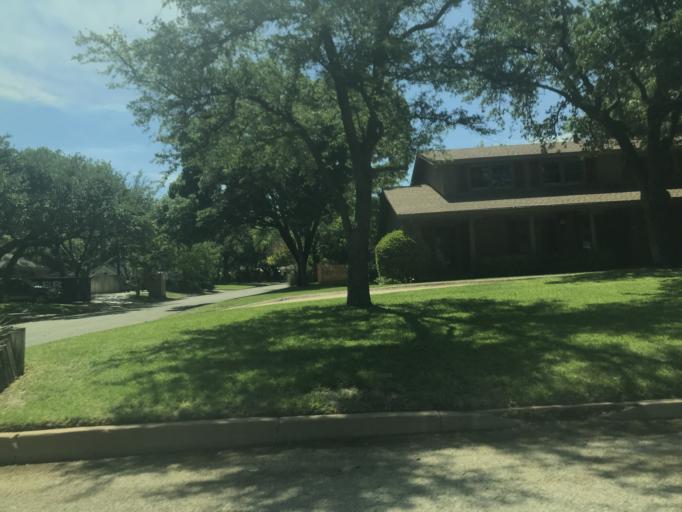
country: US
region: Texas
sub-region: Taylor County
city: Abilene
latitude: 32.4348
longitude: -99.7702
